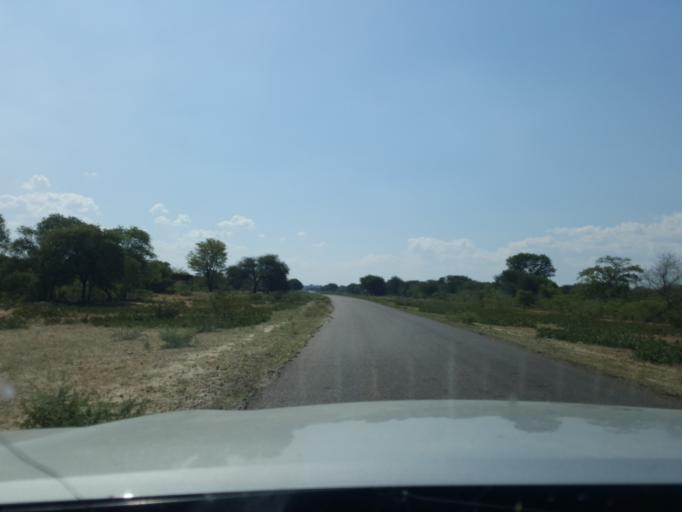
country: BW
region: North West
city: Shakawe
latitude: -18.7555
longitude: 22.1792
